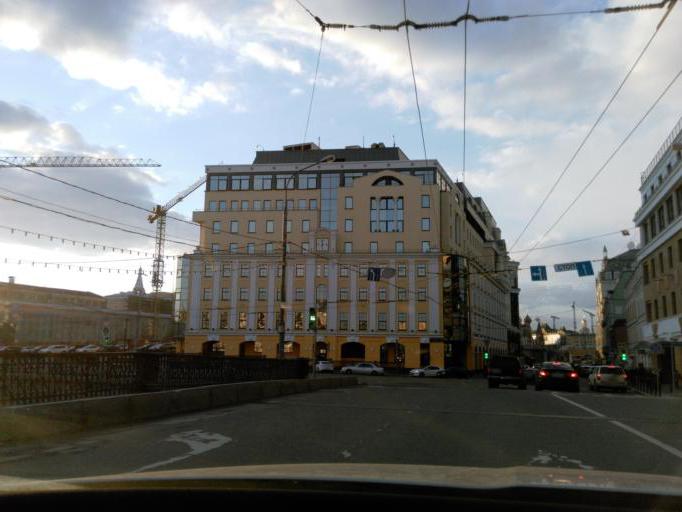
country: RU
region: Moscow
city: Moscow
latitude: 55.7462
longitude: 37.6262
